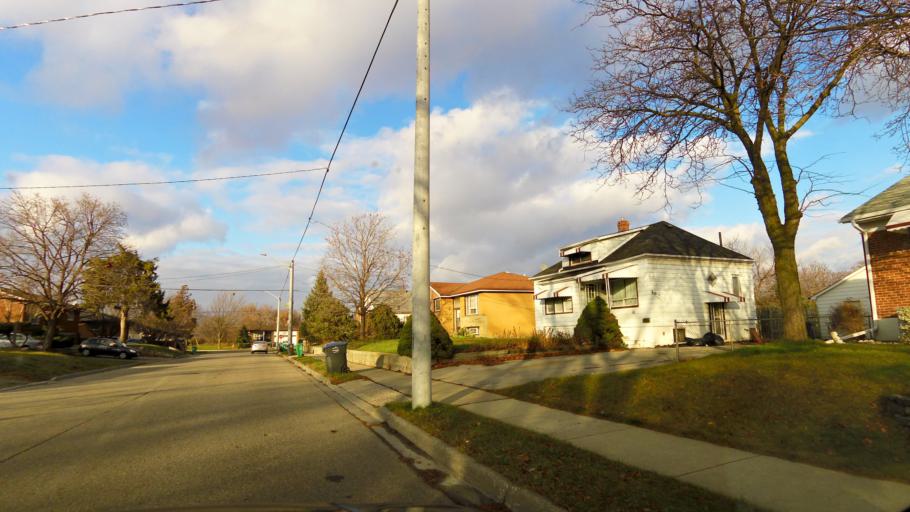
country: CA
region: Ontario
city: Etobicoke
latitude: 43.7032
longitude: -79.6476
